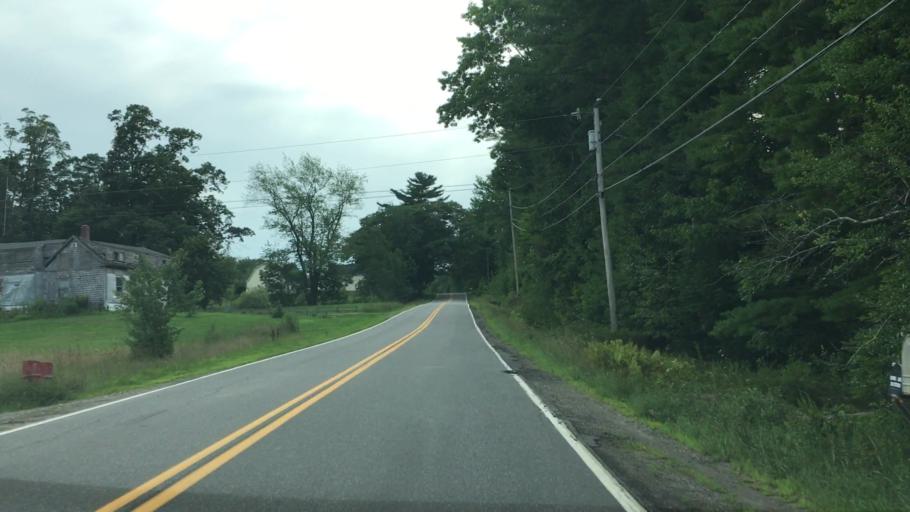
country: US
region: Maine
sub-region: Waldo County
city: Lincolnville
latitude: 44.3273
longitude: -69.0630
